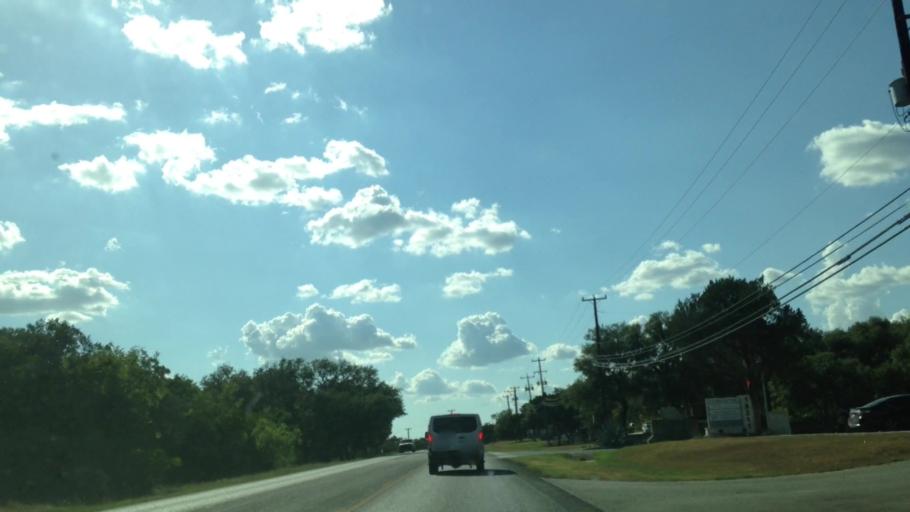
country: US
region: Texas
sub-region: Comal County
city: Garden Ridge
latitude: 29.6212
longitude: -98.2981
